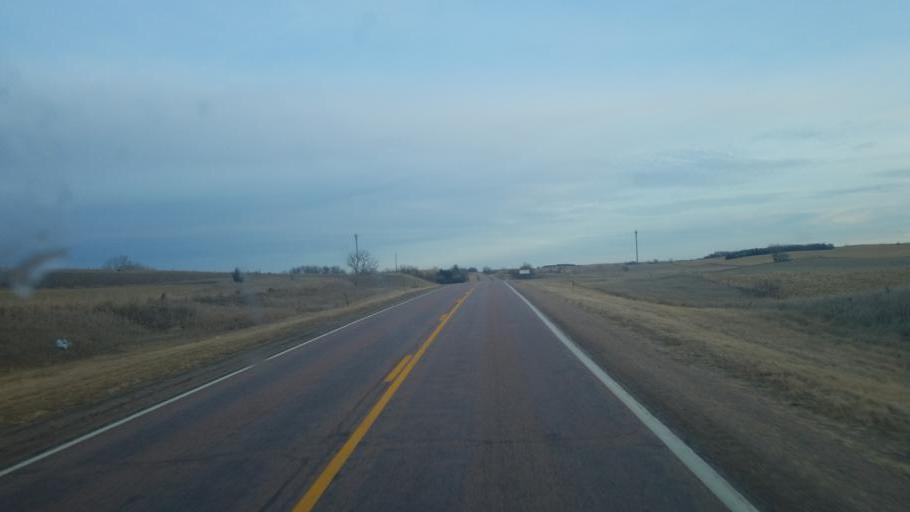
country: US
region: Nebraska
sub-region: Knox County
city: Bloomfield
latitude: 42.7278
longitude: -97.7218
